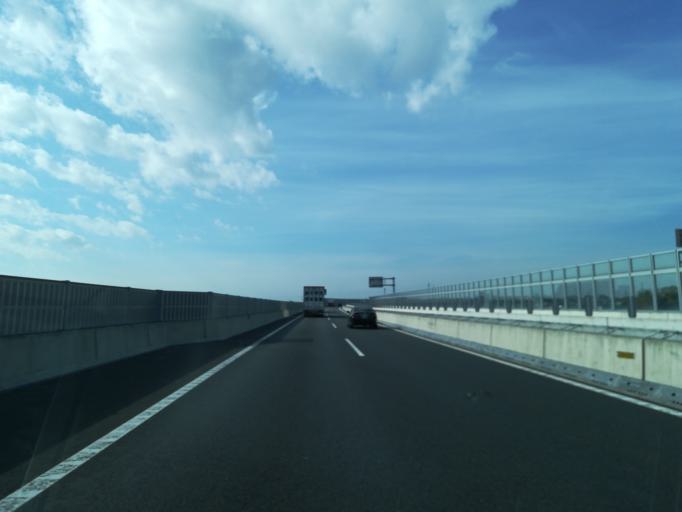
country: JP
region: Saitama
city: Satte
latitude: 36.0620
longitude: 139.7287
